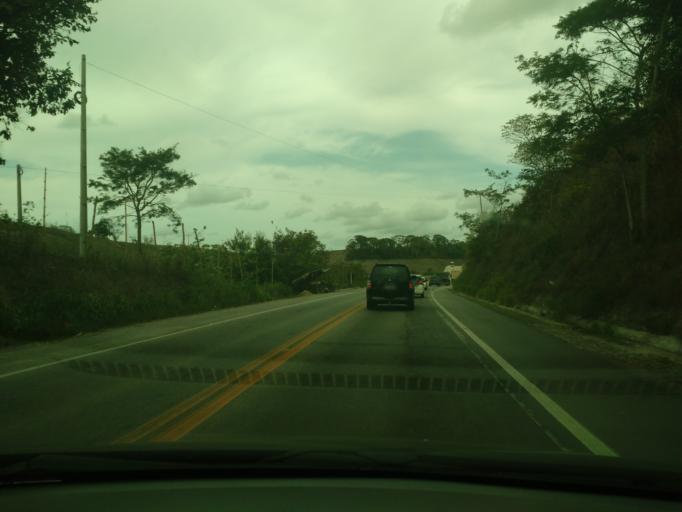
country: BR
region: Alagoas
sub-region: Messias
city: Messias
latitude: -9.3681
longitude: -35.8376
